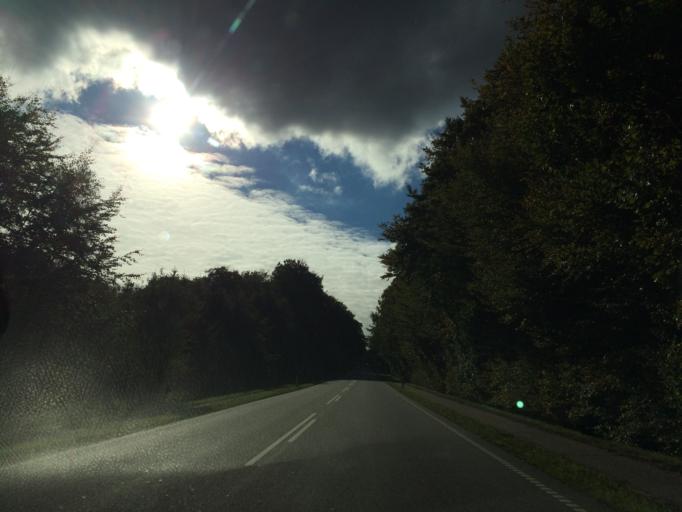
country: DK
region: Central Jutland
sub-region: Skanderborg Kommune
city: Ry
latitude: 56.0879
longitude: 9.7491
